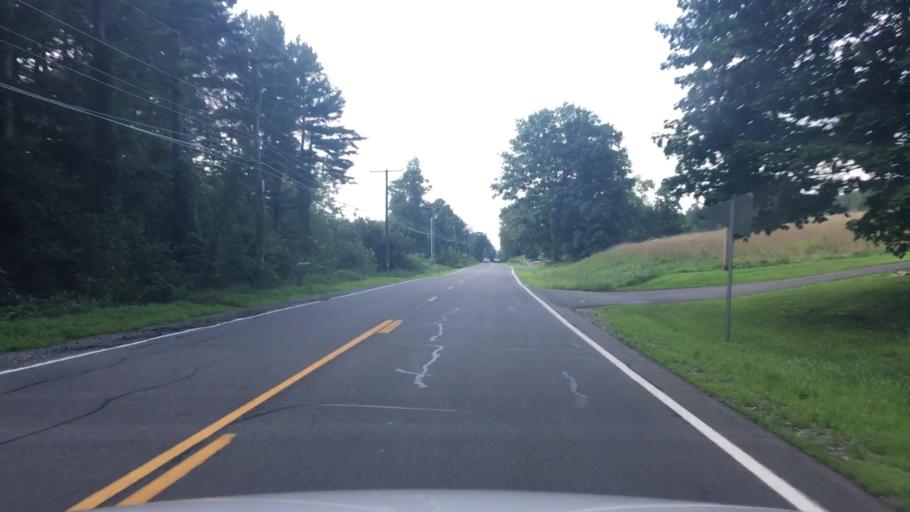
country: US
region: New Hampshire
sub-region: Rockingham County
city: Auburn
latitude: 42.9699
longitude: -71.3650
